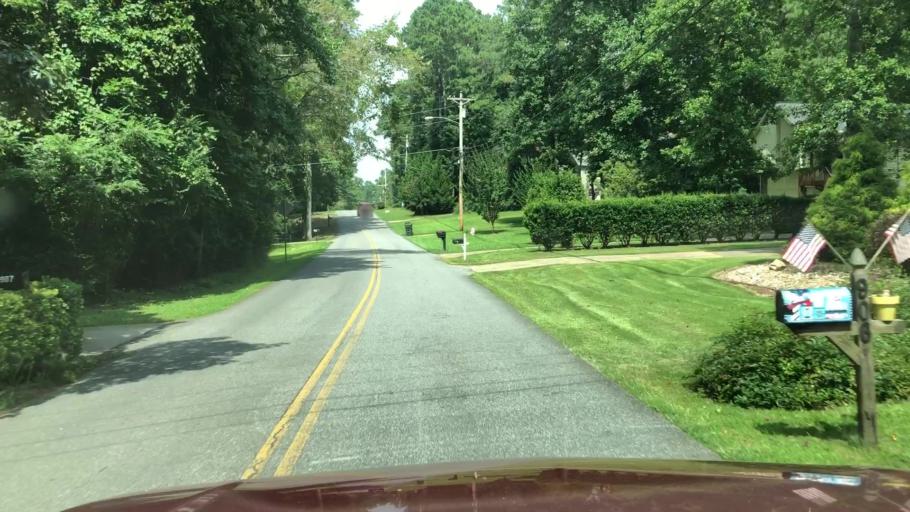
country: US
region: Georgia
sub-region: Cherokee County
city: Woodstock
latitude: 34.1471
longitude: -84.6052
